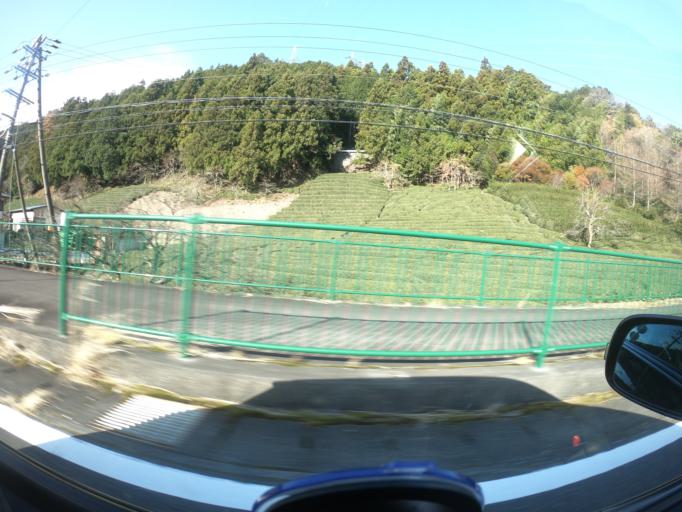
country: JP
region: Shizuoka
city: Kanaya
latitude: 35.0695
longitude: 138.1071
